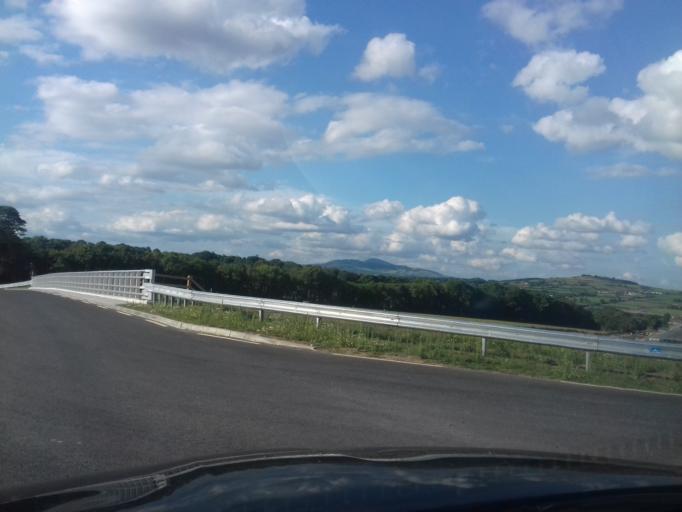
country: IE
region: Leinster
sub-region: Loch Garman
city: New Ross
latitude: 52.3734
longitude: -6.9208
